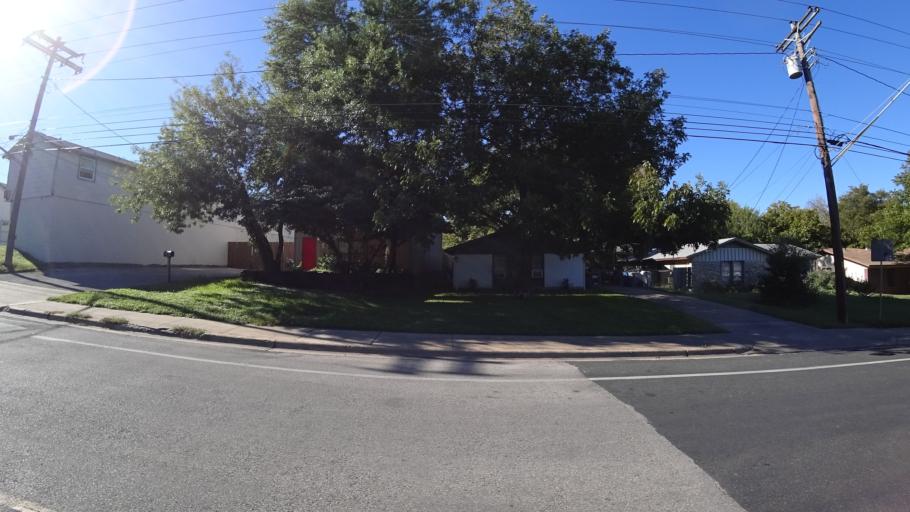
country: US
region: Texas
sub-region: Travis County
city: Austin
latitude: 30.2301
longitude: -97.7611
